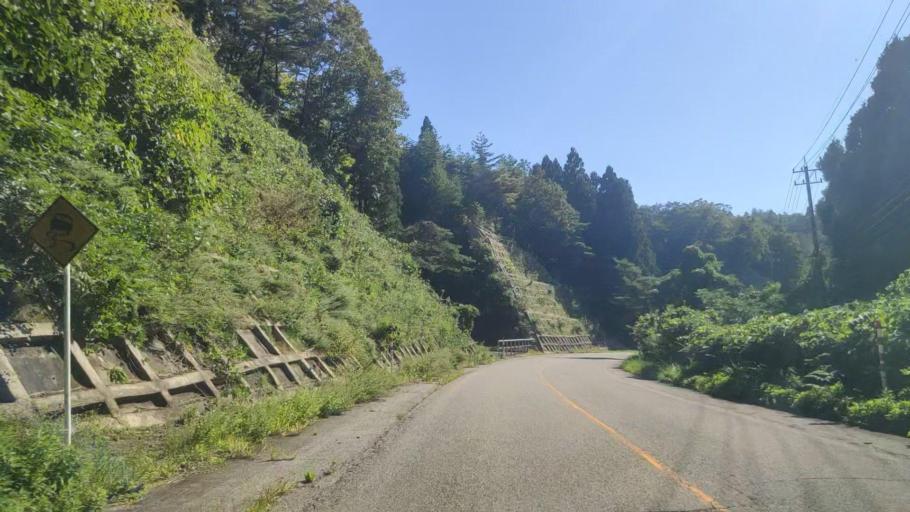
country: JP
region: Ishikawa
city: Nanao
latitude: 37.3168
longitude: 137.1649
